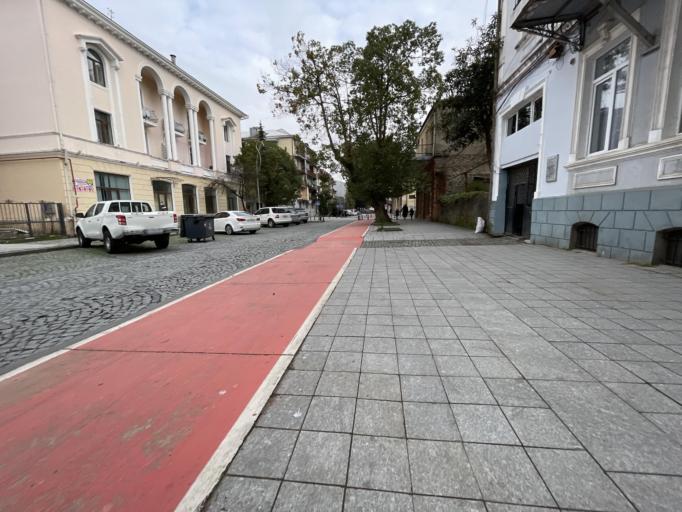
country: GE
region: Ajaria
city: Batumi
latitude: 41.6473
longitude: 41.6342
